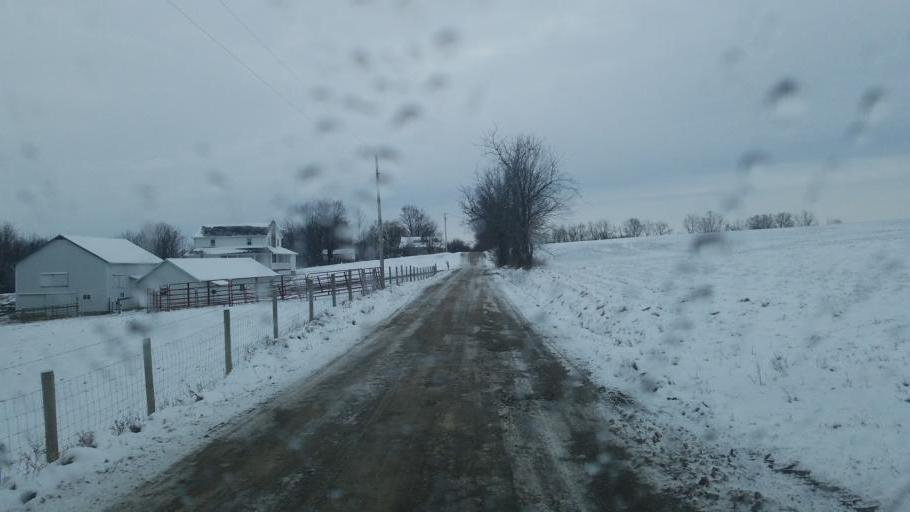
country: US
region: Ohio
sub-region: Knox County
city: Fredericktown
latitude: 40.4981
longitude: -82.6157
